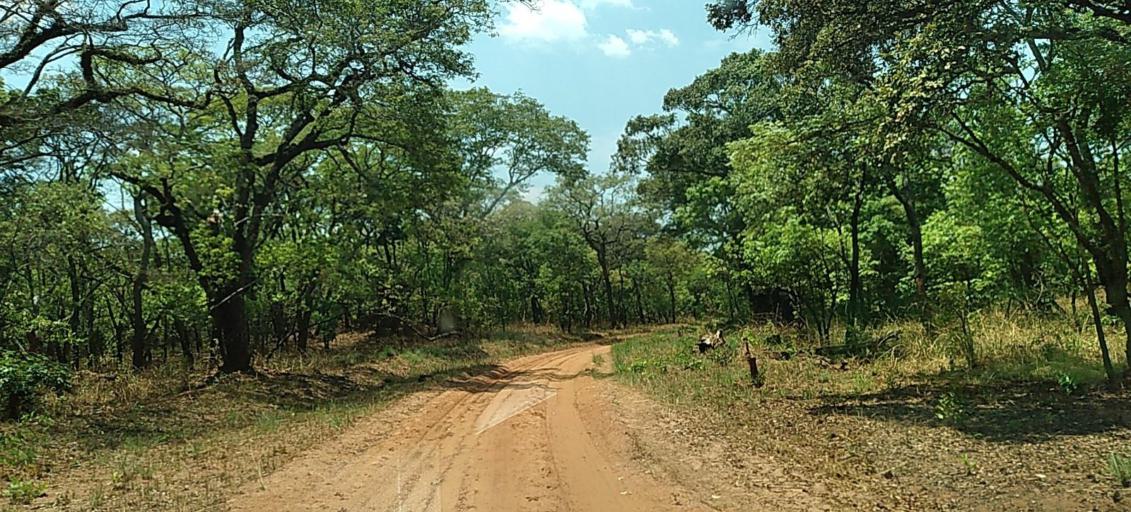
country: CD
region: Katanga
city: Kolwezi
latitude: -11.3592
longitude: 25.2063
